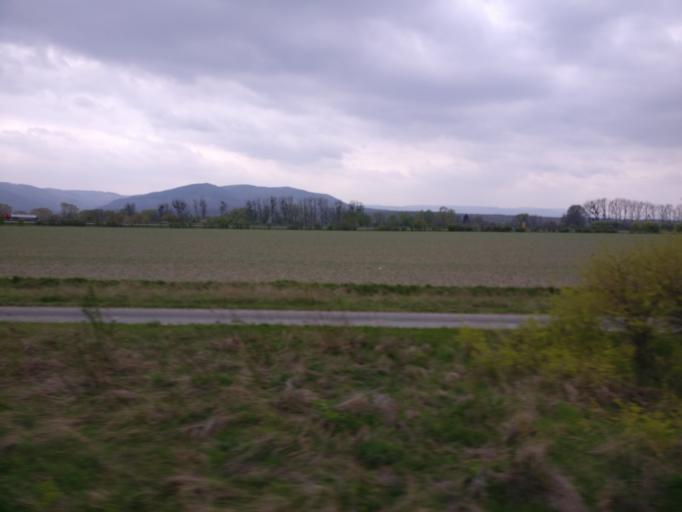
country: DE
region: Saxony-Anhalt
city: Stapelburg
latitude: 51.9138
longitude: 10.6717
